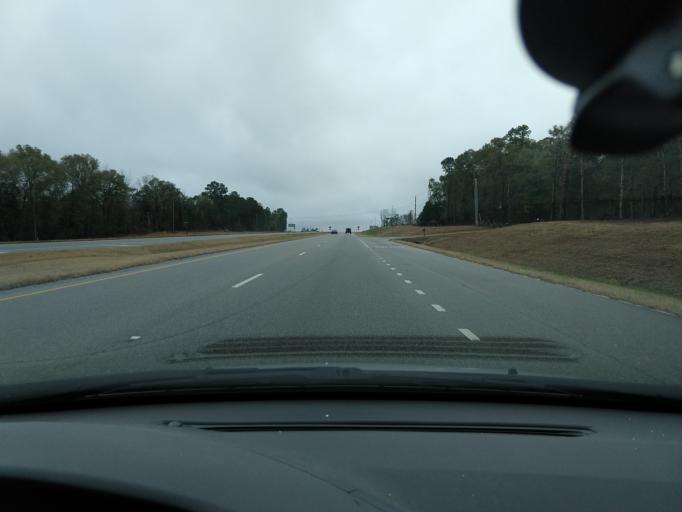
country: US
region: Alabama
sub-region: Houston County
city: Kinsey
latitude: 31.2875
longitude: -85.3661
